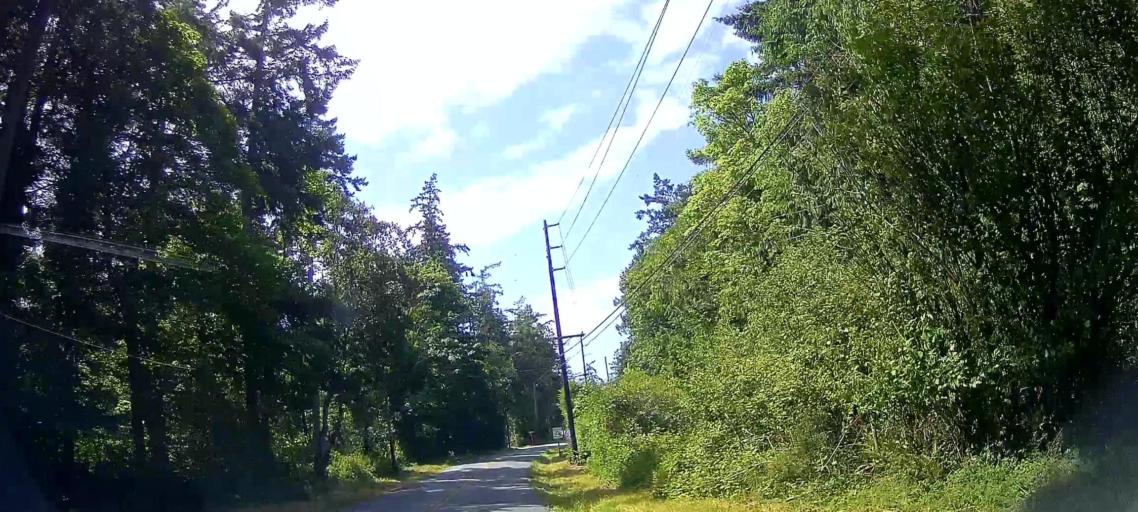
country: US
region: Washington
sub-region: Skagit County
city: Anacortes
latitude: 48.4493
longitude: -122.5670
